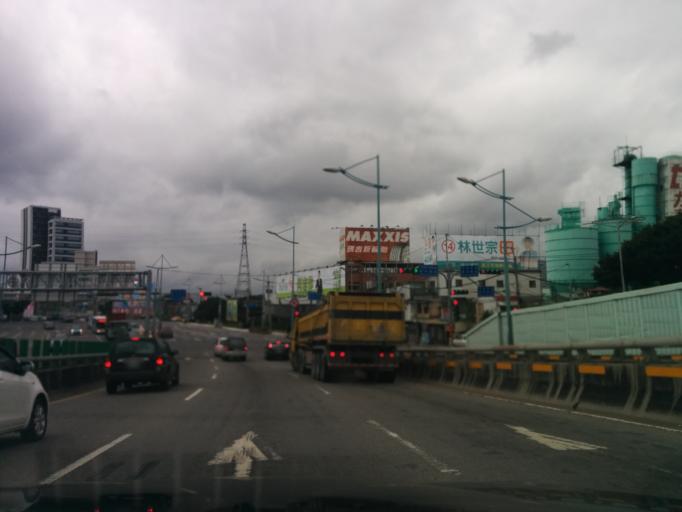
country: TW
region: Taipei
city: Taipei
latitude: 25.0954
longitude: 121.4971
